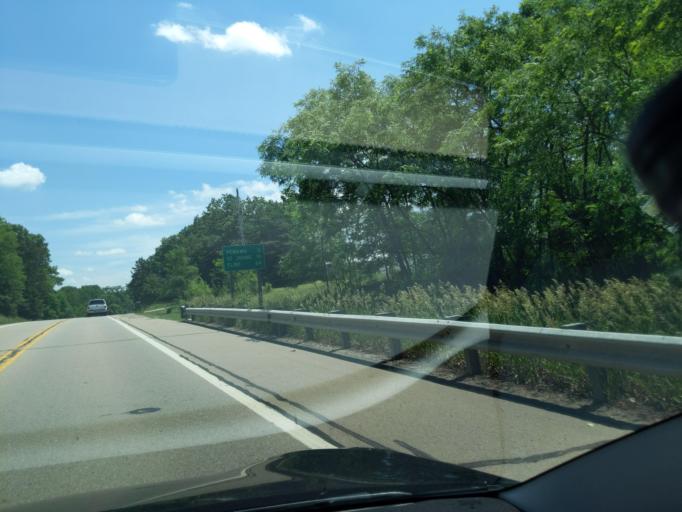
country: US
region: Michigan
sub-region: Ionia County
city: Portland
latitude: 43.0020
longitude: -84.9308
